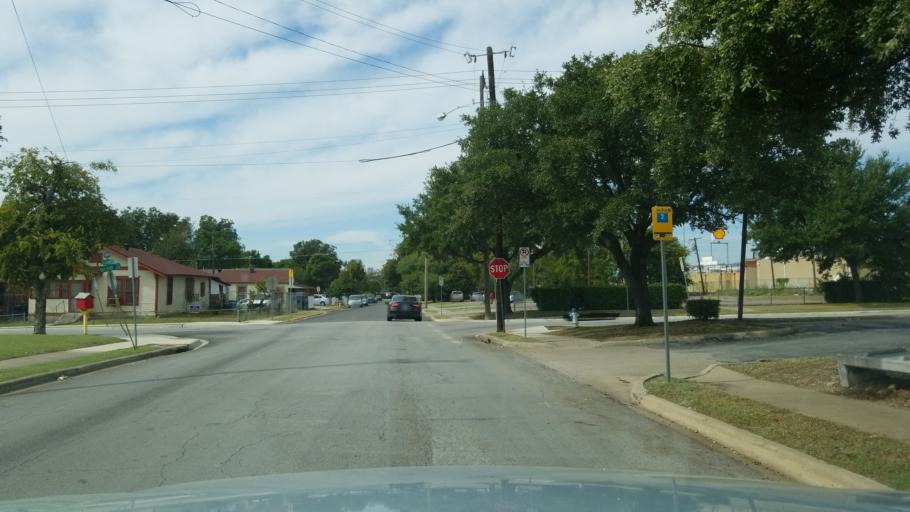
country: US
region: Texas
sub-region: Dallas County
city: Dallas
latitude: 32.7900
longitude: -96.7440
